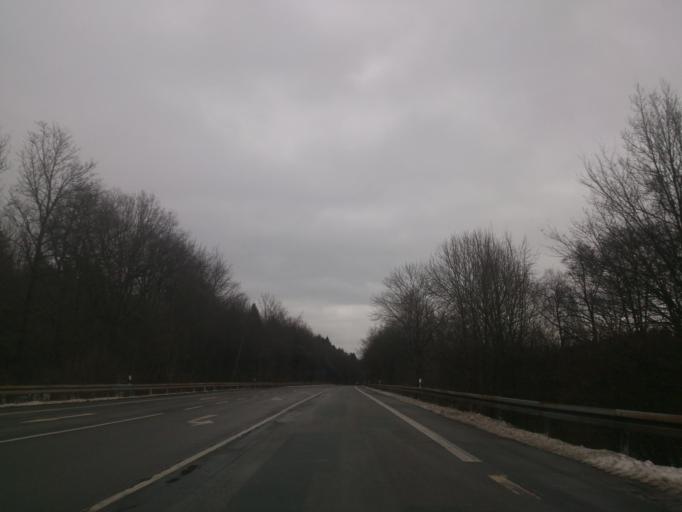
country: DE
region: North Rhine-Westphalia
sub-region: Regierungsbezirk Detmold
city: Bad Driburg
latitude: 51.6880
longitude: 8.9738
